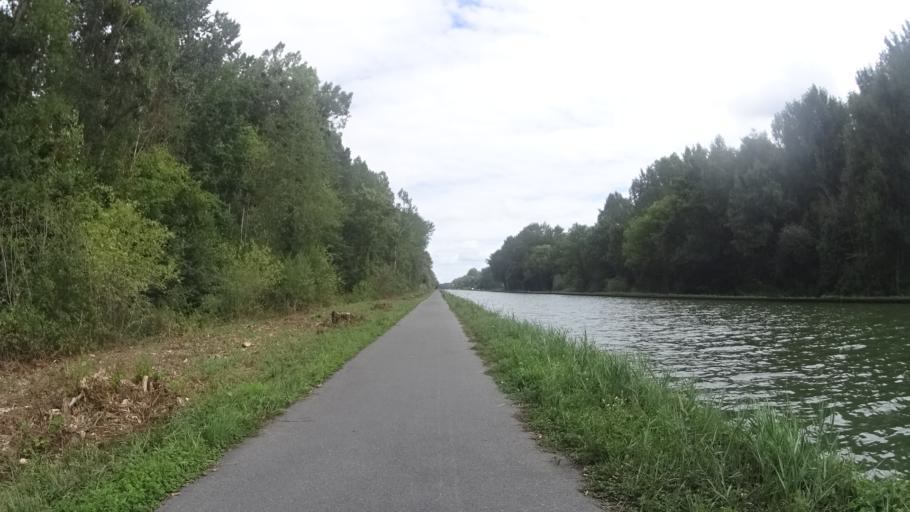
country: FR
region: Picardie
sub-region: Departement de l'Aisne
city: Blerancourt
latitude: 49.5791
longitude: 3.1303
